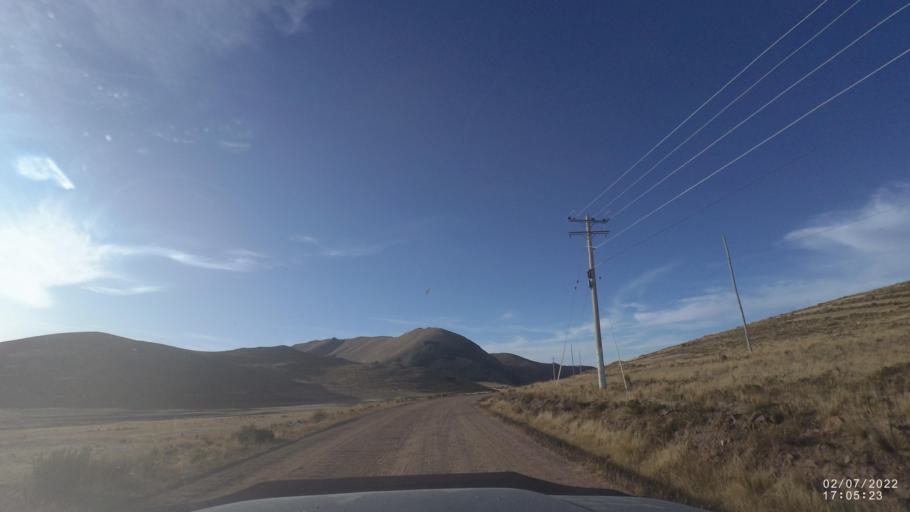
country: BO
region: Cochabamba
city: Irpa Irpa
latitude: -17.9074
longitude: -66.5598
